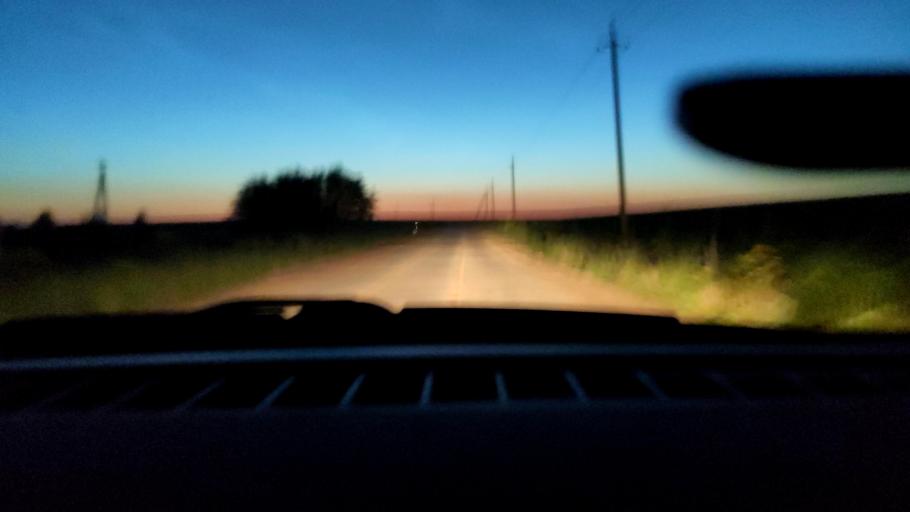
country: RU
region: Perm
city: Kultayevo
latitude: 57.8483
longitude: 55.9898
